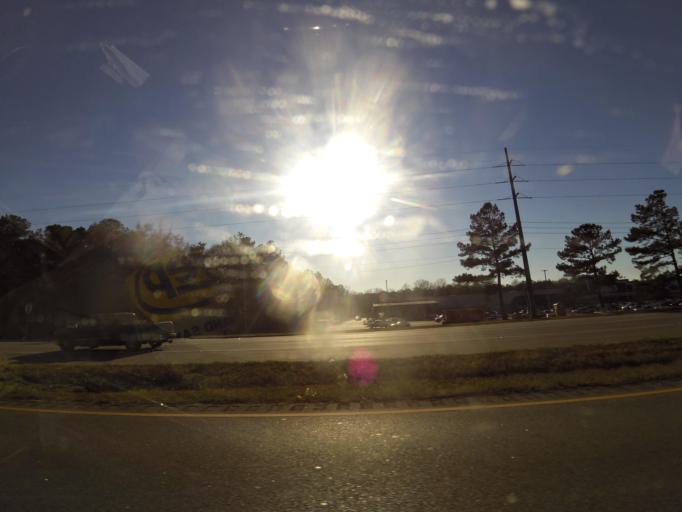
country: US
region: Alabama
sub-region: Houston County
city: Dothan
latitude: 31.2061
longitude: -85.4223
